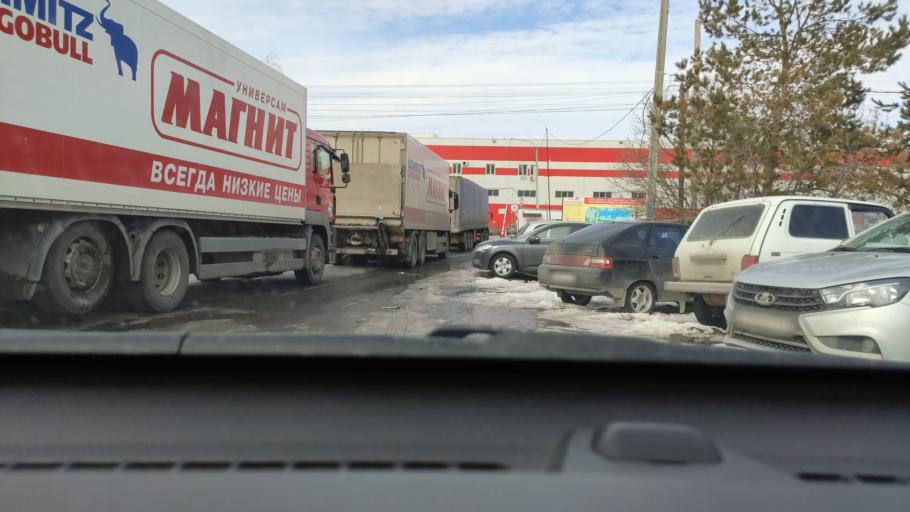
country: RU
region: Samara
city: Zhigulevsk
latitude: 53.5558
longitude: 49.5071
